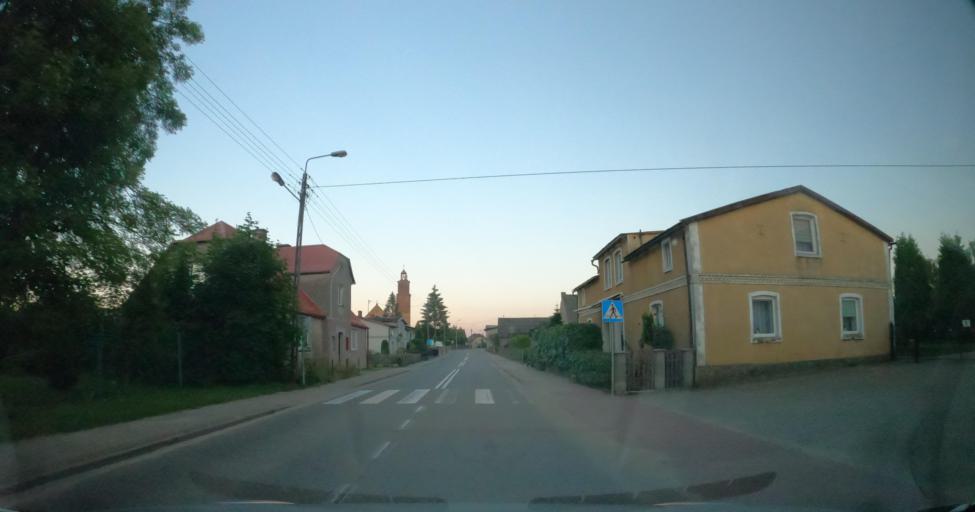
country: PL
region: Pomeranian Voivodeship
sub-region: Powiat wejherowski
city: Linia
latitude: 54.4563
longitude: 18.0218
